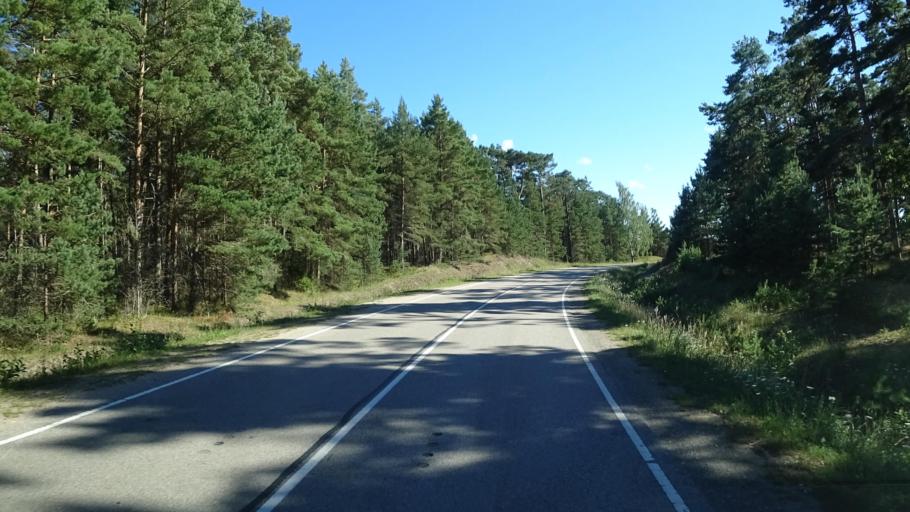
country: LV
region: Rojas
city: Roja
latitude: 57.7528
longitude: 22.5961
